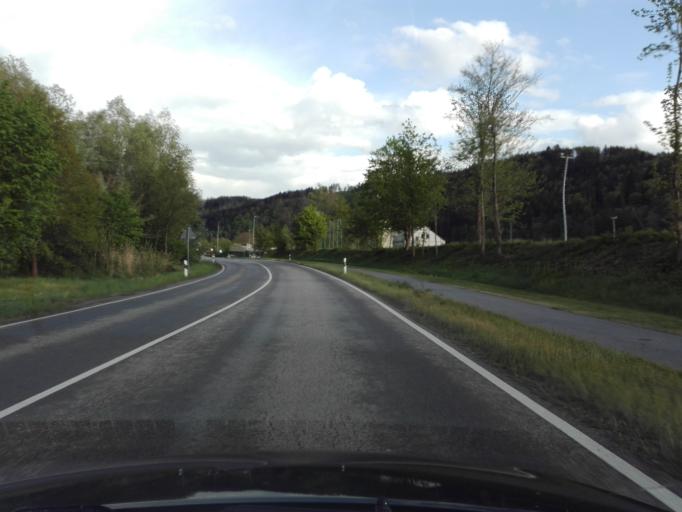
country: DE
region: Bavaria
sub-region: Lower Bavaria
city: Obernzell
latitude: 48.5583
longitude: 13.6234
